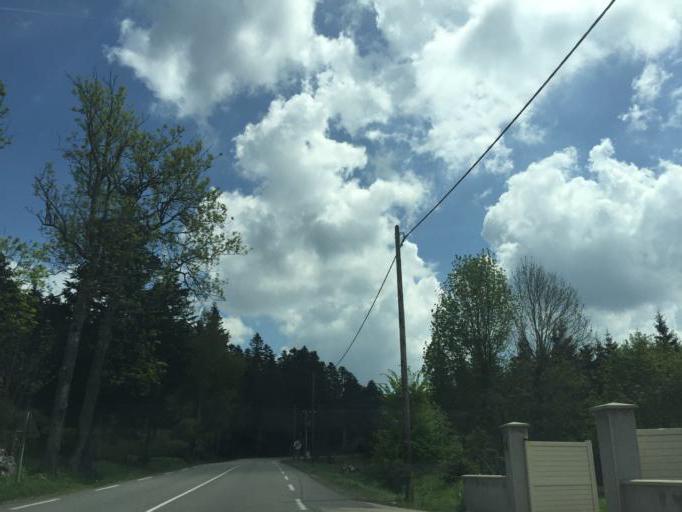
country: FR
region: Rhone-Alpes
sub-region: Departement de la Loire
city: Saint-Genest-Malifaux
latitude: 45.3486
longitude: 4.4808
